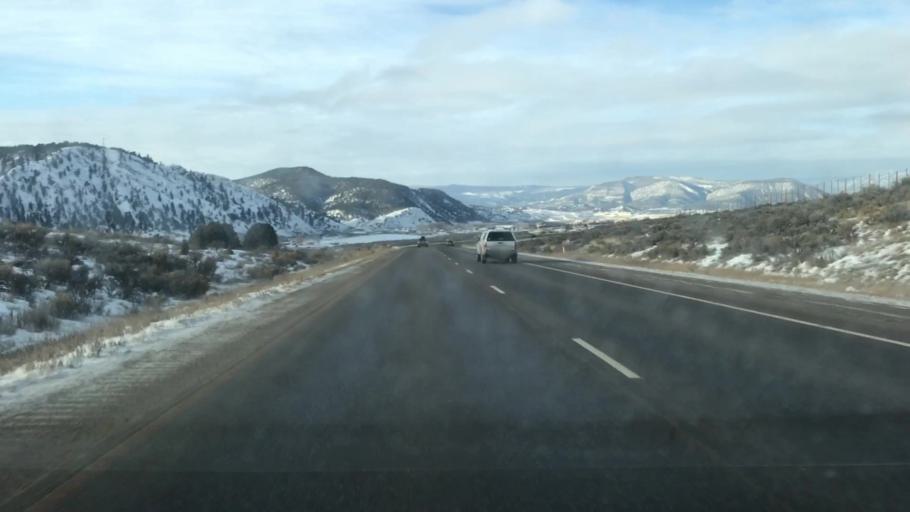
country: US
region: Colorado
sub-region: Eagle County
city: Eagle
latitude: 39.6555
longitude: -106.8467
